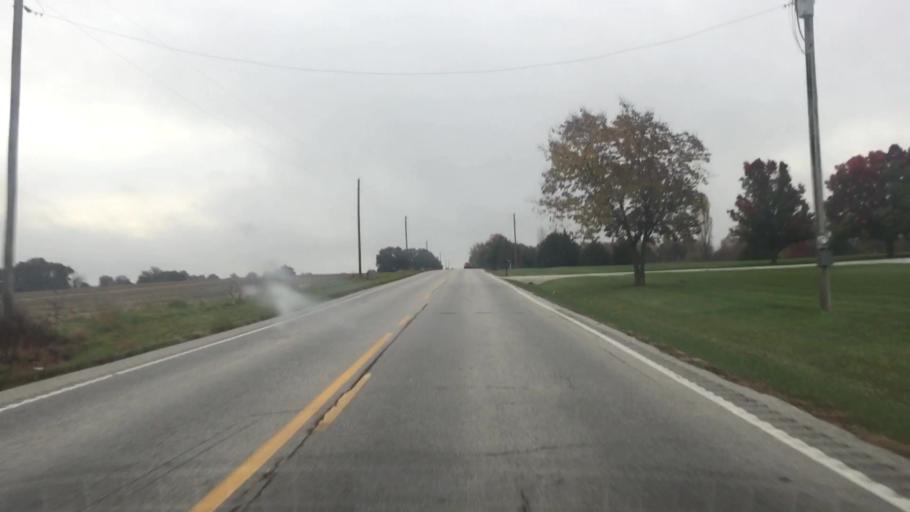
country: US
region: Missouri
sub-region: Boone County
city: Columbia
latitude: 38.9207
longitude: -92.1993
